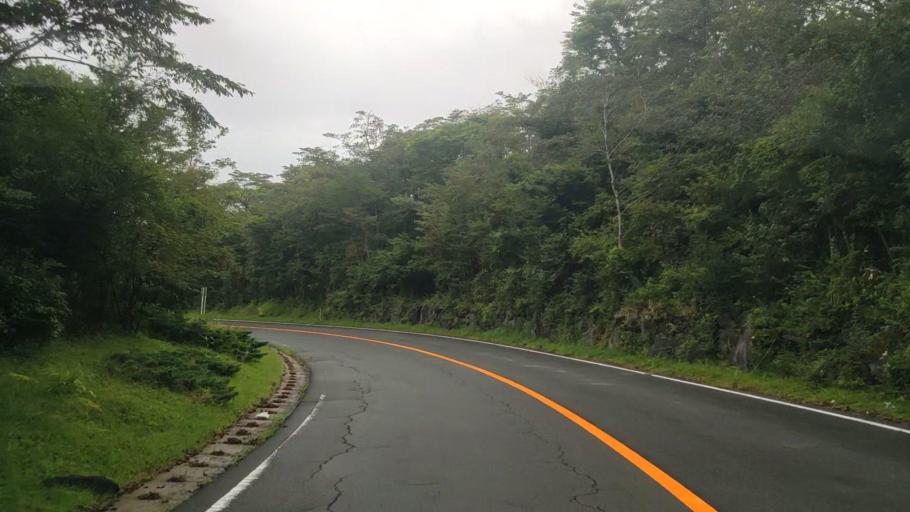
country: JP
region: Shizuoka
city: Fuji
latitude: 35.2887
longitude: 138.7767
